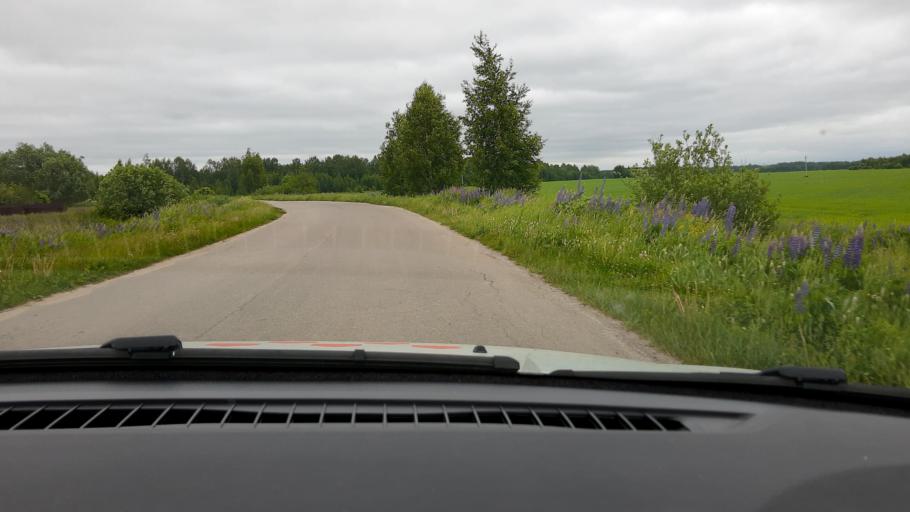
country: RU
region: Nizjnij Novgorod
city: Sitniki
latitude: 56.5204
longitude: 44.0432
